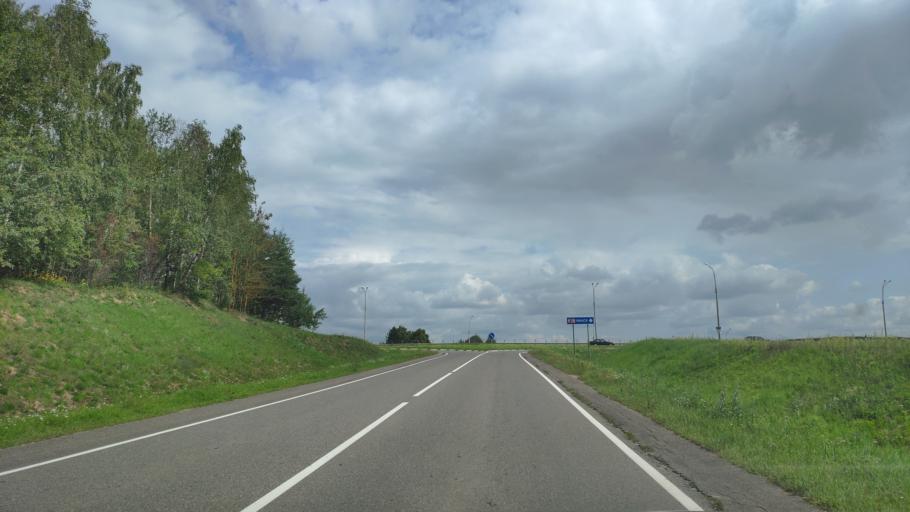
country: BY
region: Minsk
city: Zaslawye
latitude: 54.0074
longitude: 27.3073
